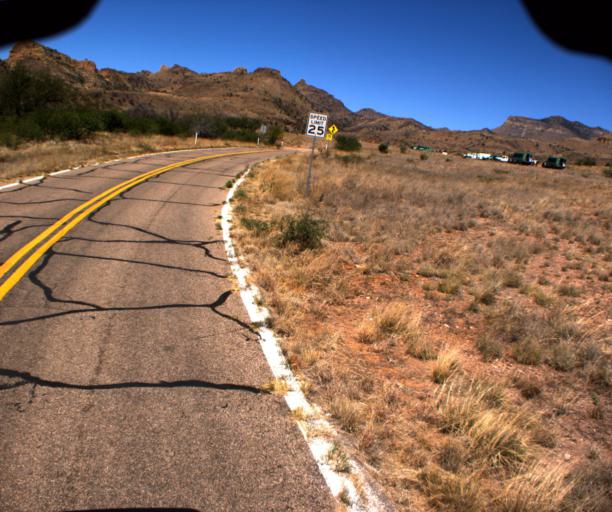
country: US
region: Arizona
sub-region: Santa Cruz County
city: Rio Rico
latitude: 31.4015
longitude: -111.0885
